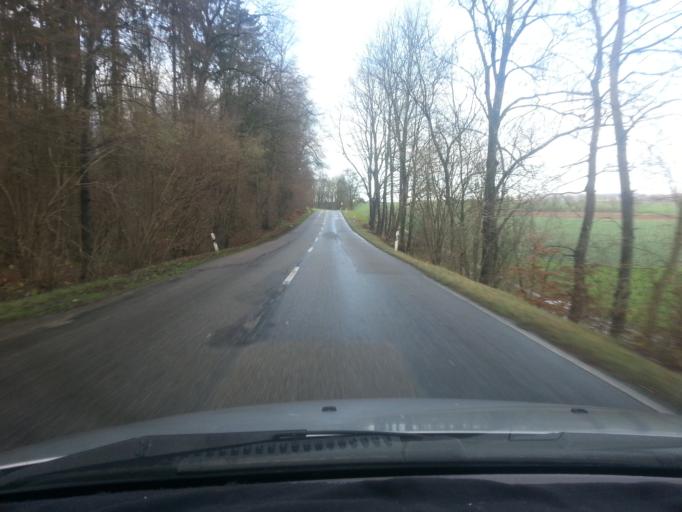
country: DE
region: Baden-Wuerttemberg
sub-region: Regierungsbezirk Stuttgart
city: Eppingen
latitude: 49.1597
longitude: 8.8779
